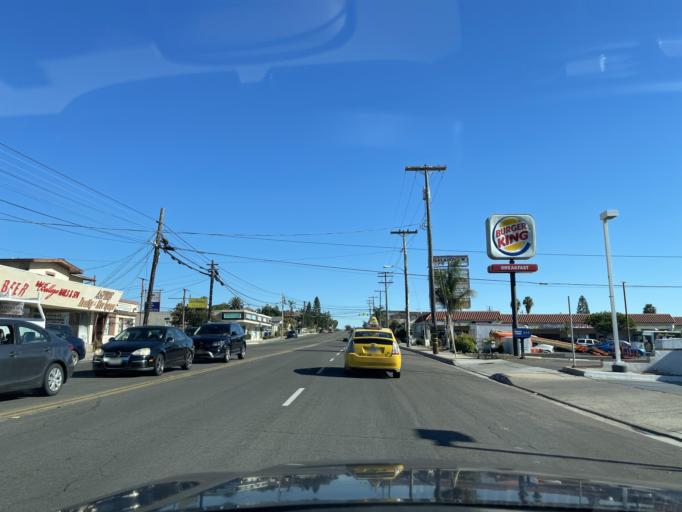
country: US
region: California
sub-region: San Diego County
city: National City
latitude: 32.6782
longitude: -117.0984
